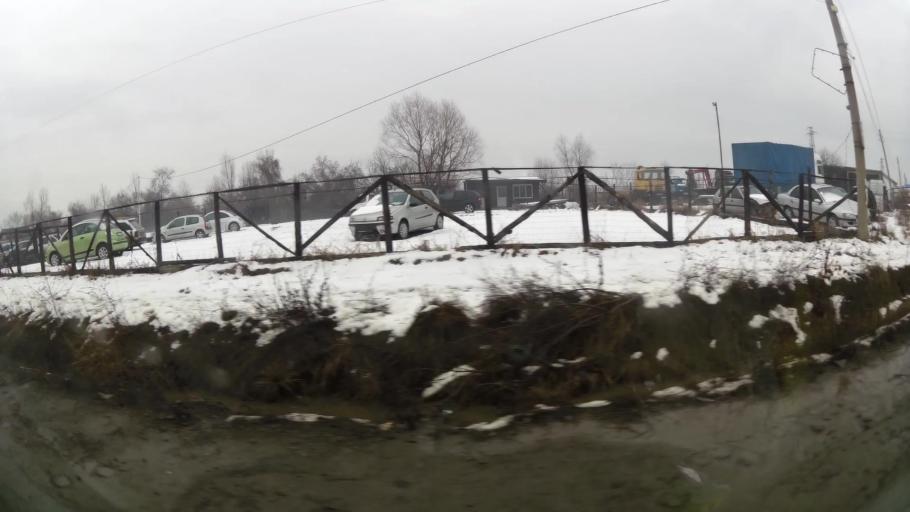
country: BG
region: Sofiya
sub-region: Obshtina Bozhurishte
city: Bozhurishte
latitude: 42.6888
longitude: 23.2309
